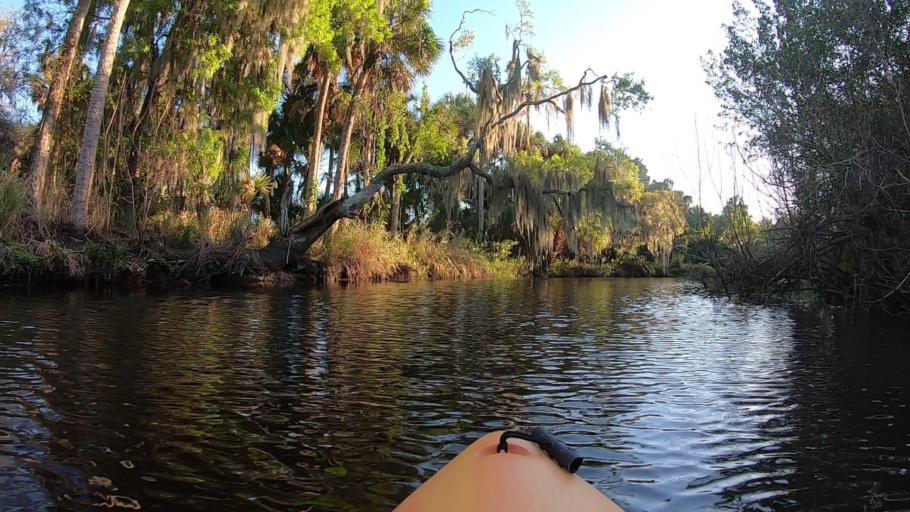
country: US
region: Florida
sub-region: Manatee County
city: Memphis
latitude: 27.5921
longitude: -82.5547
